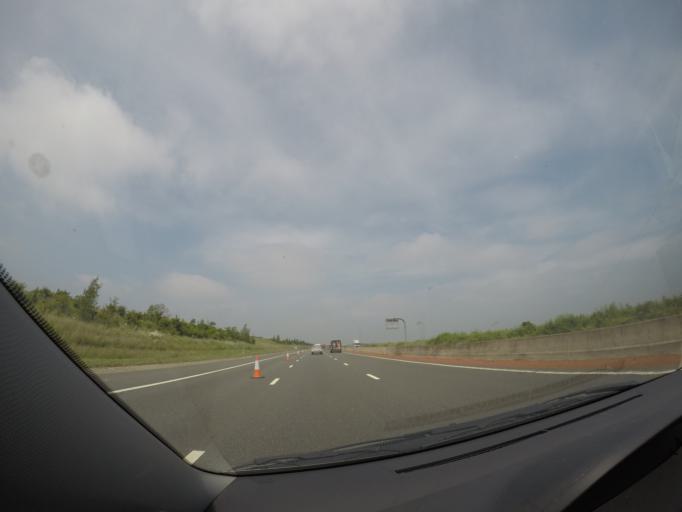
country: GB
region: England
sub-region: North Yorkshire
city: Ripon
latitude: 54.2335
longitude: -1.4948
